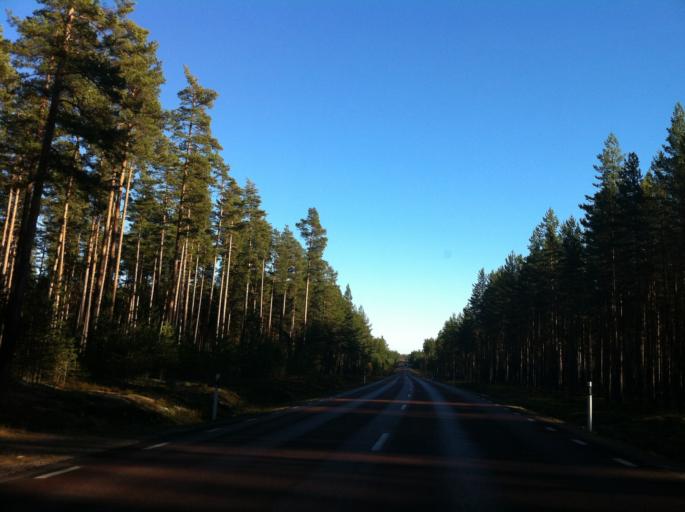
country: SE
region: Dalarna
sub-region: Leksand Municipality
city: Siljansnas
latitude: 60.9369
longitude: 14.7576
